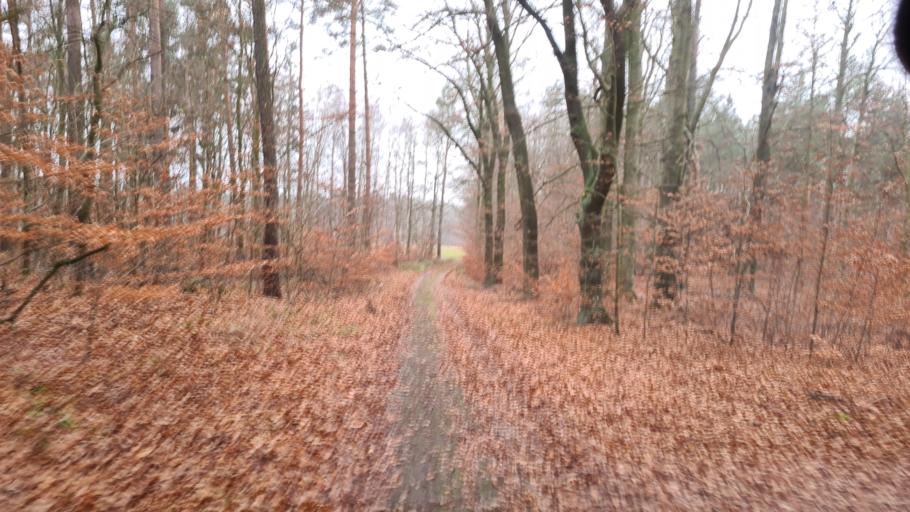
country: DE
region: Brandenburg
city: Doberlug-Kirchhain
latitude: 51.6312
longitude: 13.5299
